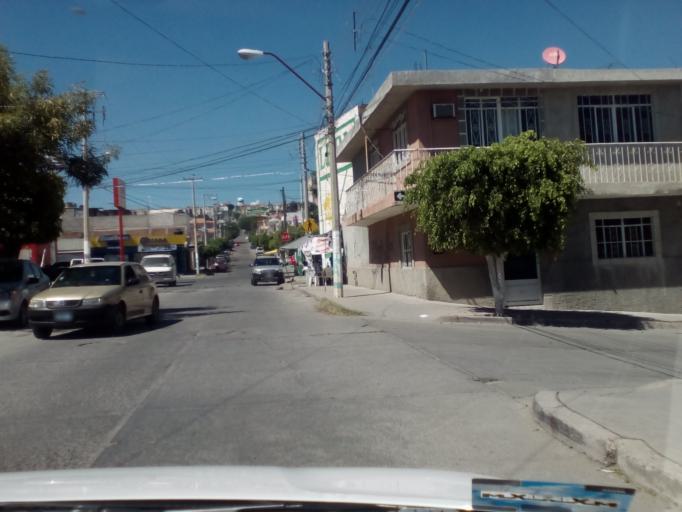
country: MX
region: Guanajuato
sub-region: Leon
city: Ejido la Joya
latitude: 21.1247
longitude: -101.7133
